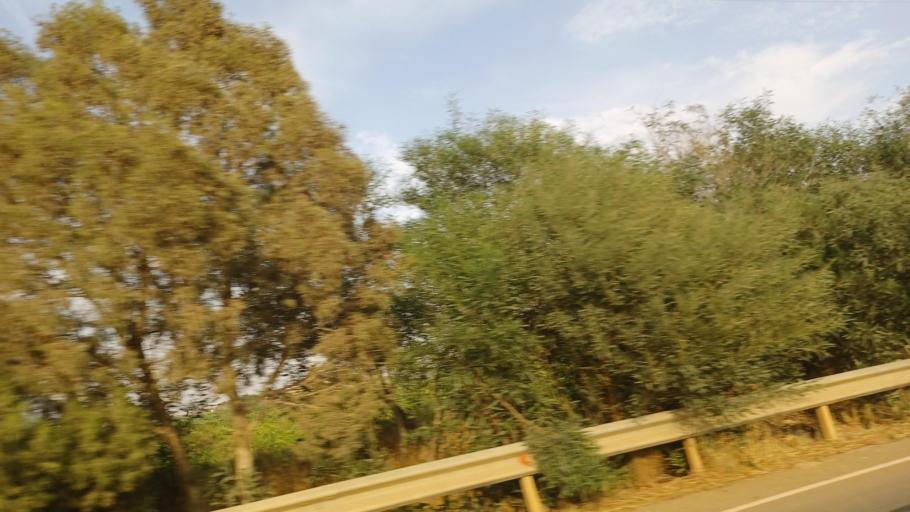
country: CY
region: Ammochostos
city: Frenaros
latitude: 35.0616
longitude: 33.8936
